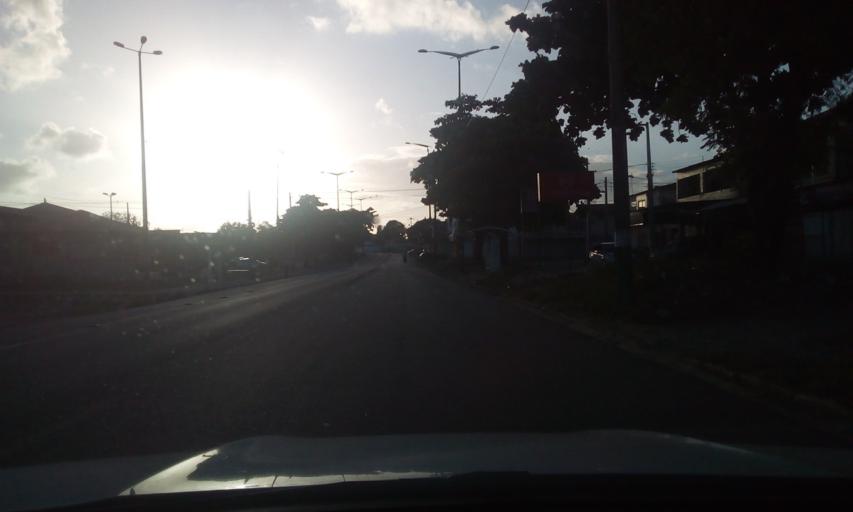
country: BR
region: Paraiba
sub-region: Conde
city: Conde
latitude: -7.2018
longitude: -34.8492
